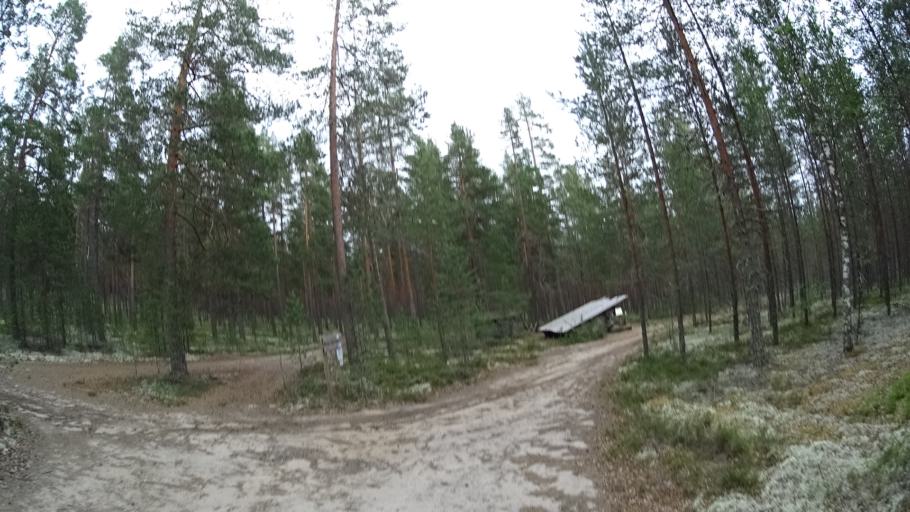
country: FI
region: Satakunta
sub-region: Pohjois-Satakunta
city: Jaemijaervi
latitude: 61.7682
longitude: 22.7490
